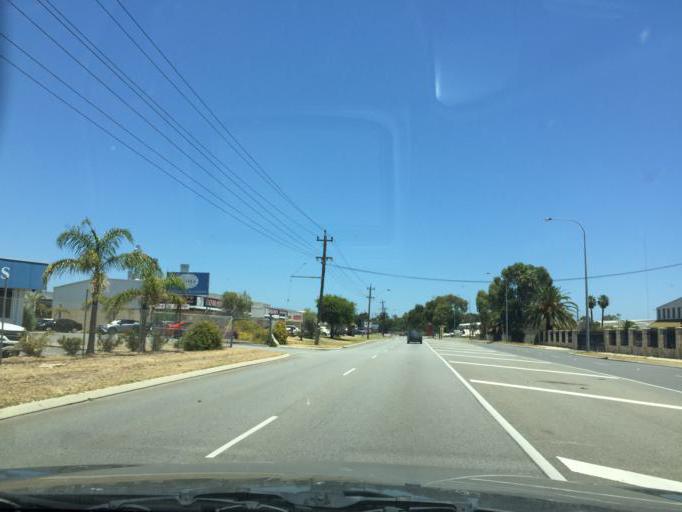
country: AU
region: Western Australia
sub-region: Canning
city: Canning Vale
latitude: -32.0581
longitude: 115.9135
